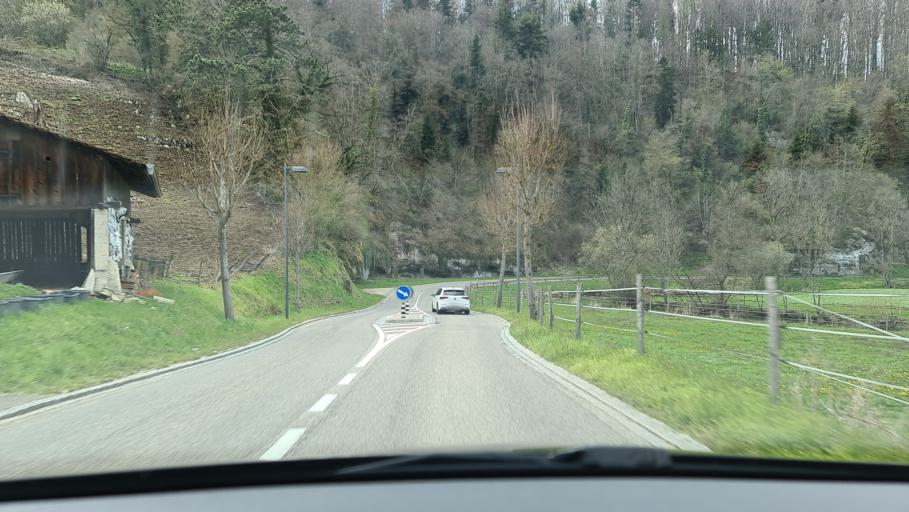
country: CH
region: Jura
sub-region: Porrentruy District
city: Porrentruy
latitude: 47.4417
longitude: 7.0554
